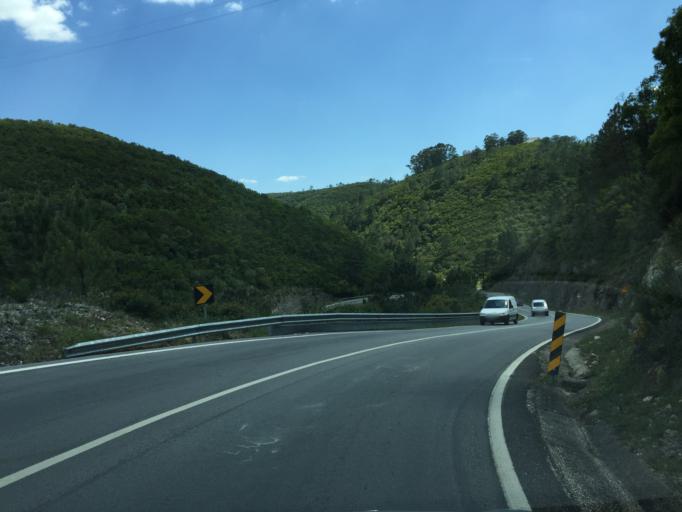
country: PT
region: Santarem
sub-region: Ourem
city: Fatima
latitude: 39.6337
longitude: -8.6524
